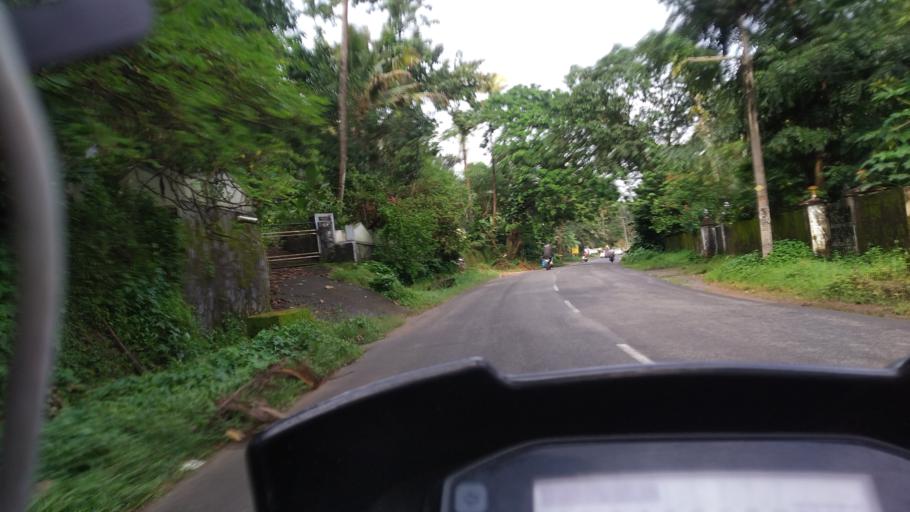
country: IN
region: Kerala
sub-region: Ernakulam
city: Kotamangalam
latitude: 10.0502
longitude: 76.7238
